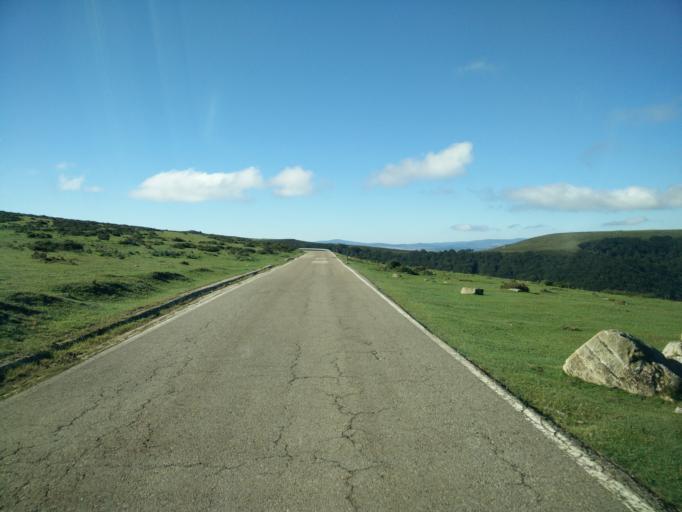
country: ES
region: Cantabria
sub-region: Provincia de Cantabria
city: San Pedro del Romeral
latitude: 43.0495
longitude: -3.8502
